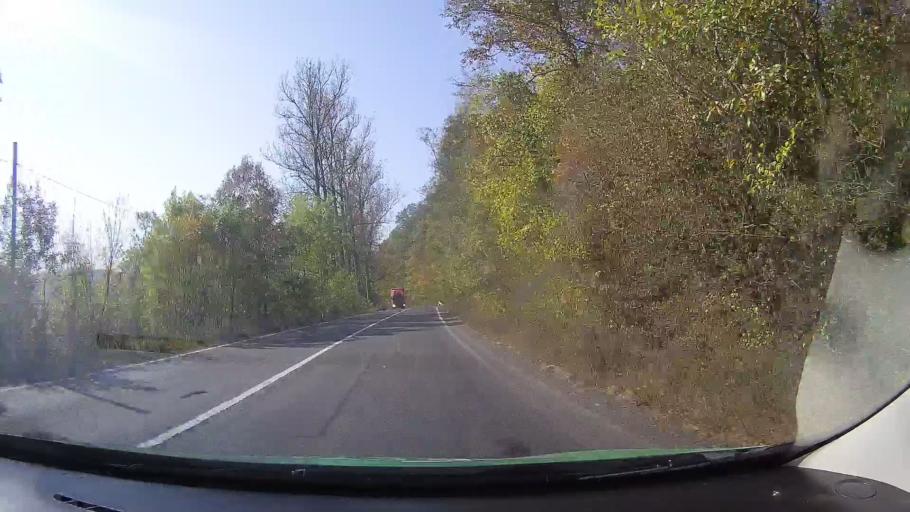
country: RO
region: Arad
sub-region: Comuna Petris
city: Petris
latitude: 46.0082
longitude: 22.3434
